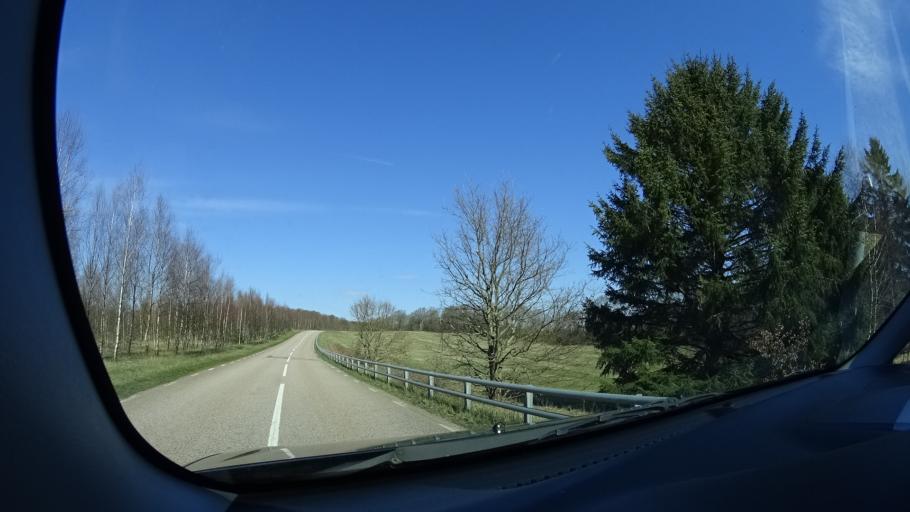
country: SE
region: Skane
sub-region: Klippans Kommun
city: Klippan
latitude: 56.1050
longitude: 13.1003
